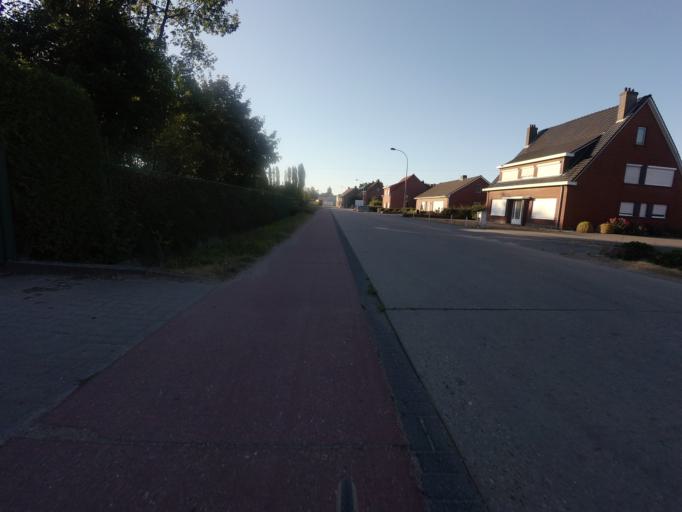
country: BE
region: Flanders
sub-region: Provincie Antwerpen
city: Brecht
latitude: 51.3413
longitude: 4.6834
